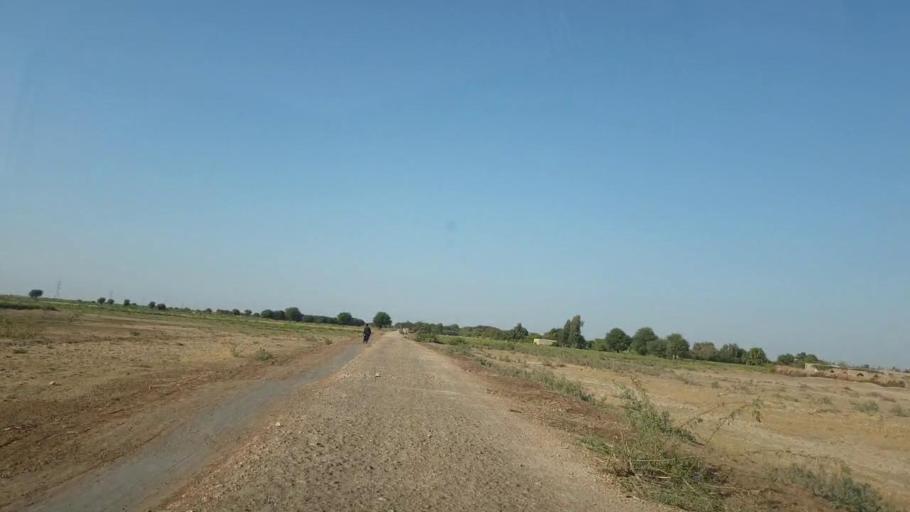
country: PK
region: Sindh
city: Kunri
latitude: 25.0446
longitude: 69.4420
